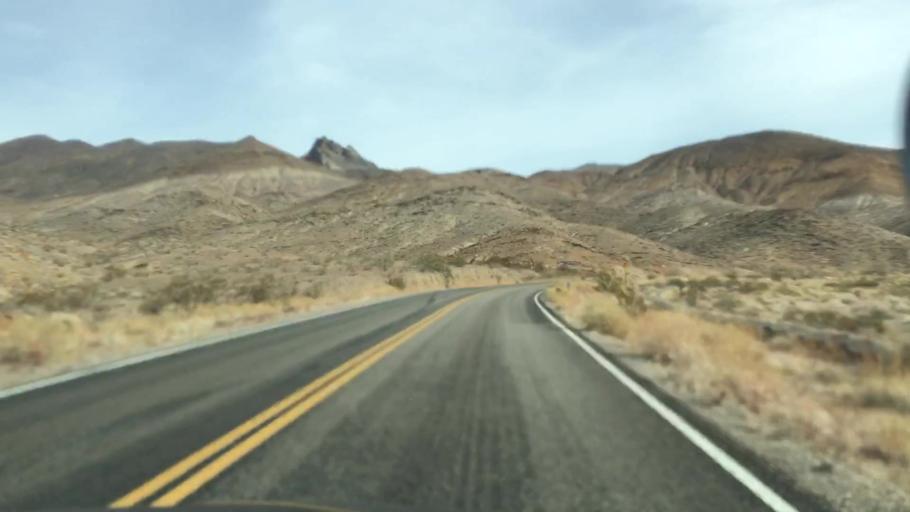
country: US
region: Nevada
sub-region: Nye County
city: Beatty
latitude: 36.7467
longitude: -116.9541
